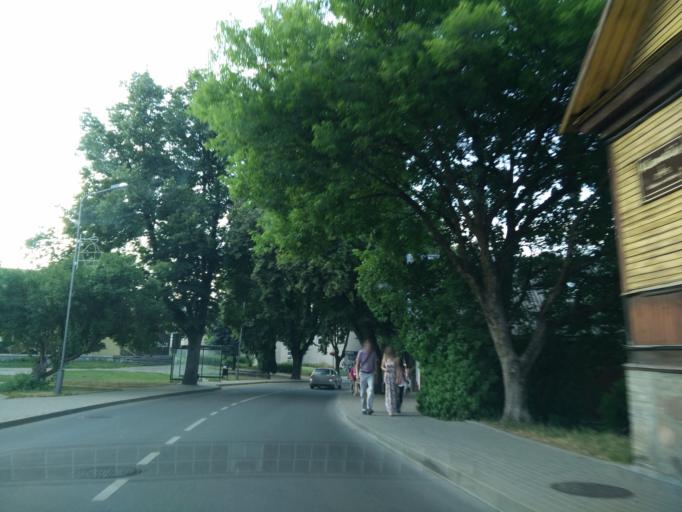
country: LT
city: Trakai
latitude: 54.6419
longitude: 24.9329
